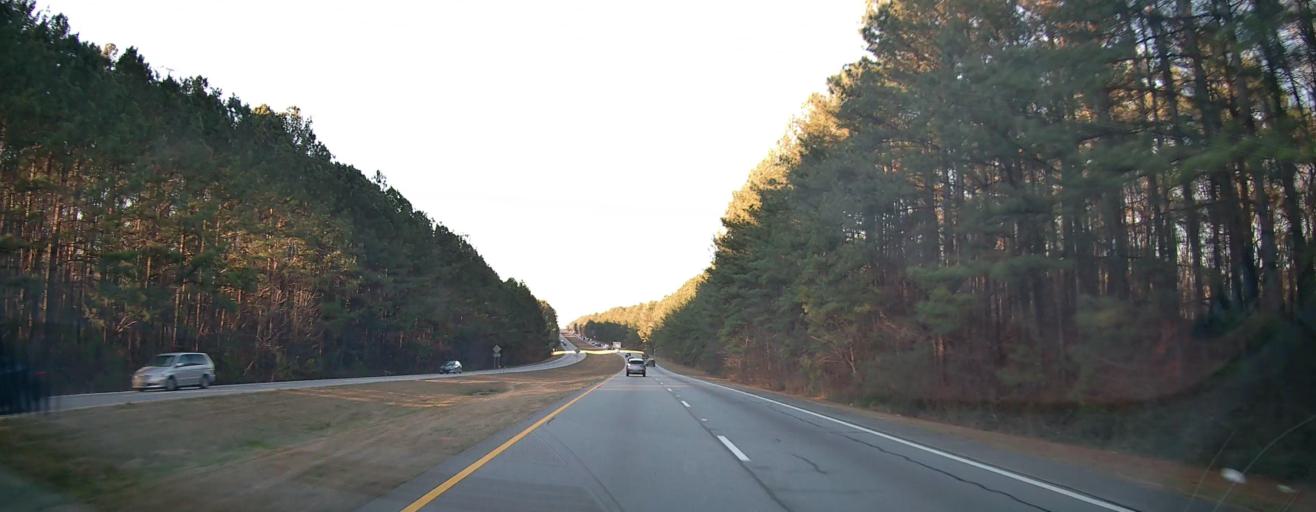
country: US
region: Georgia
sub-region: Fayette County
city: Tyrone
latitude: 33.4647
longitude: -84.5871
